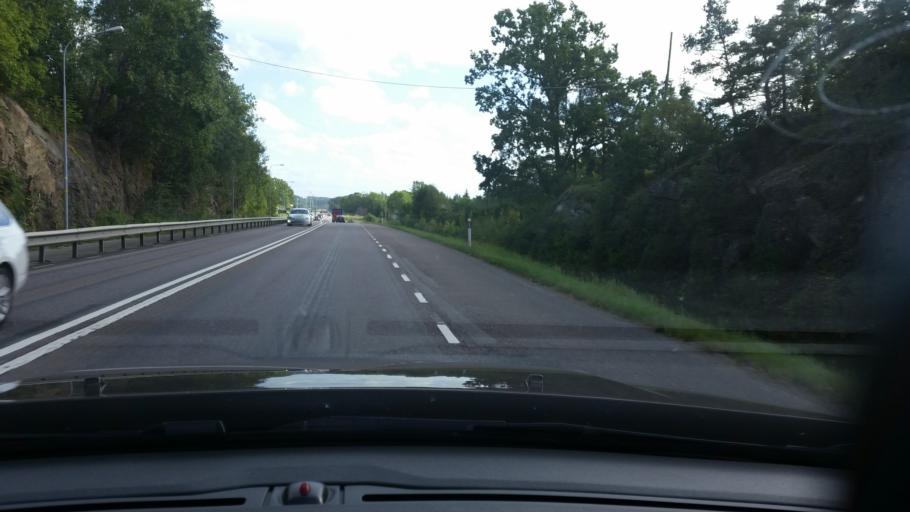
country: SE
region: Vaestra Goetaland
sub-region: Lilla Edets Kommun
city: Lilla Edet
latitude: 58.0999
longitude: 12.1522
